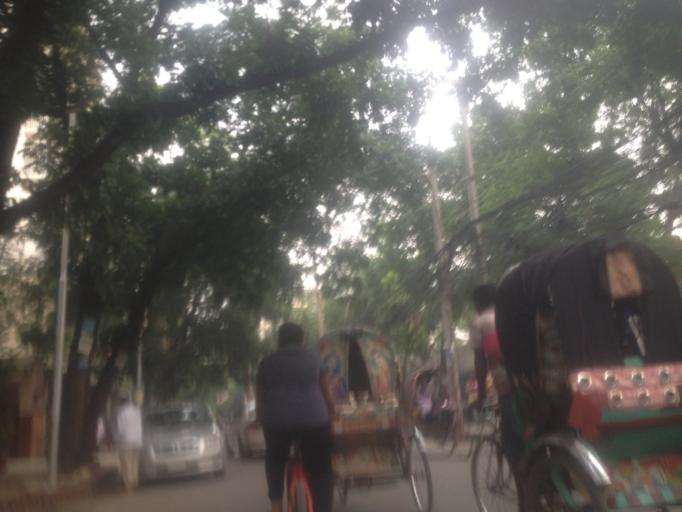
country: BD
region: Dhaka
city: Azimpur
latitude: 23.7496
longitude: 90.3719
